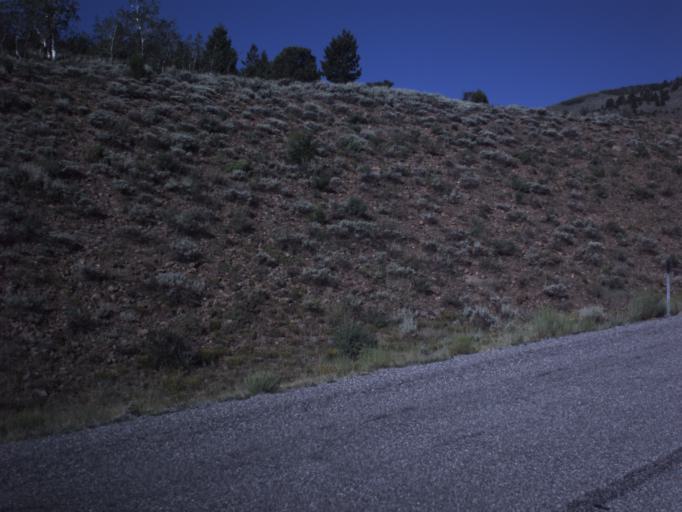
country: US
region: Utah
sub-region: Wayne County
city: Loa
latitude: 38.5998
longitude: -111.4627
